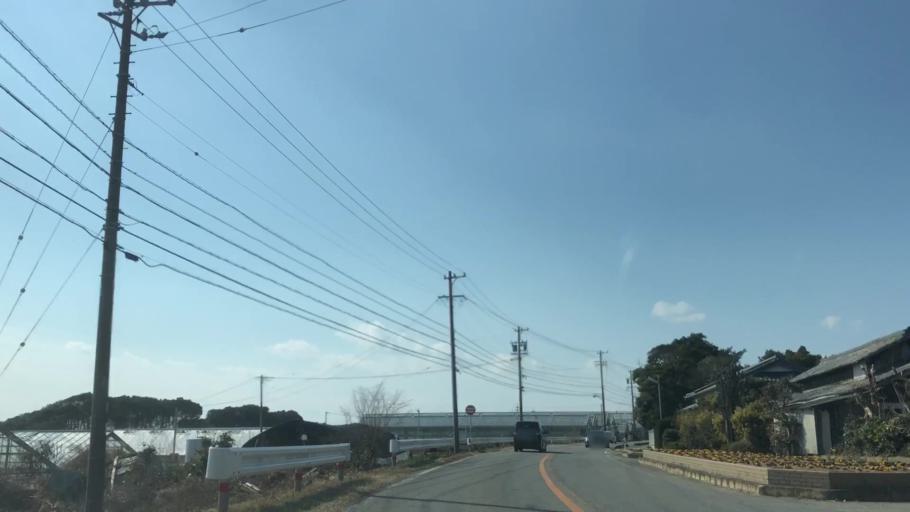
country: JP
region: Aichi
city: Tahara
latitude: 34.5900
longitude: 137.1096
